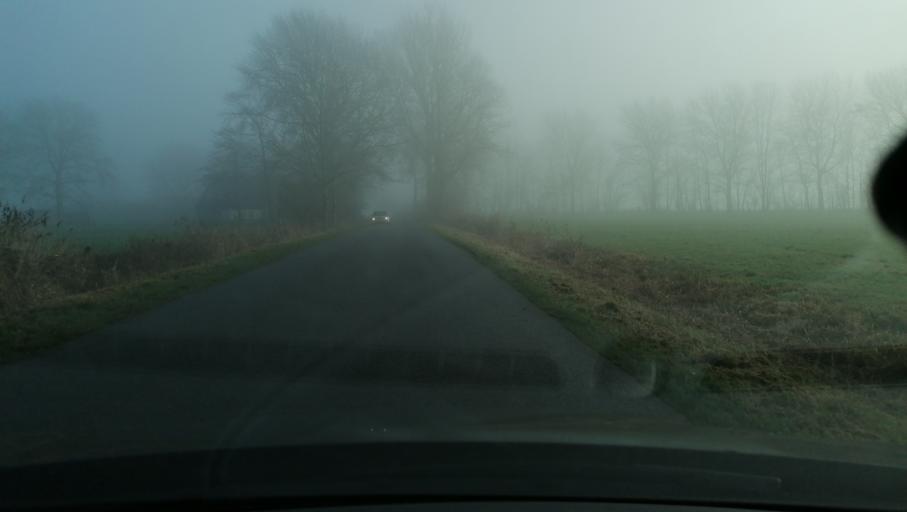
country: DE
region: Schleswig-Holstein
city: Epenwohrden
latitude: 54.1012
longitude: 9.0492
